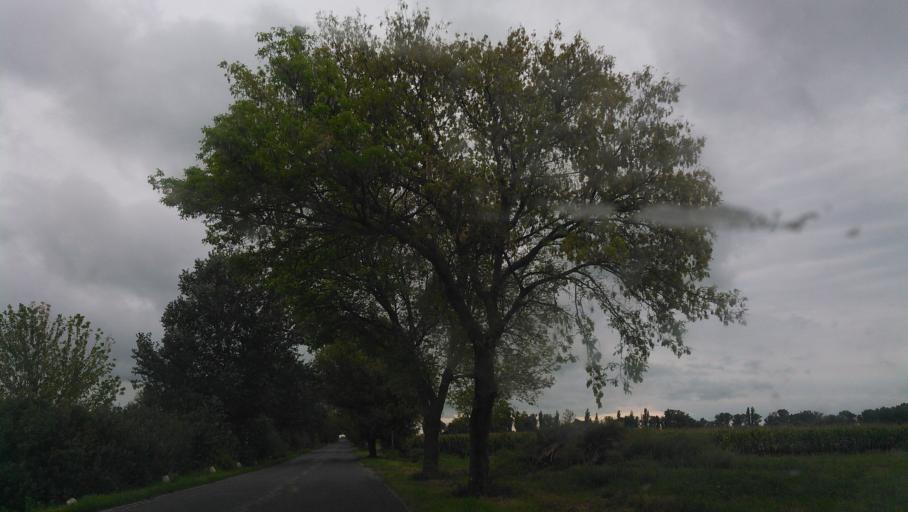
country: SK
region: Trnavsky
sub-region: Okres Dunajska Streda
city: Velky Meder
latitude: 47.9042
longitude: 17.7831
